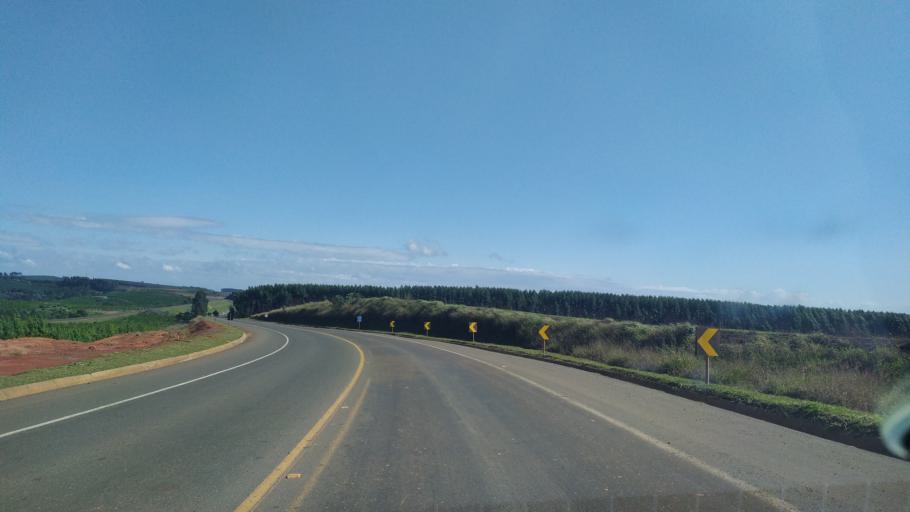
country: BR
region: Parana
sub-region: Telemaco Borba
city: Telemaco Borba
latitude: -24.2383
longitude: -50.7615
